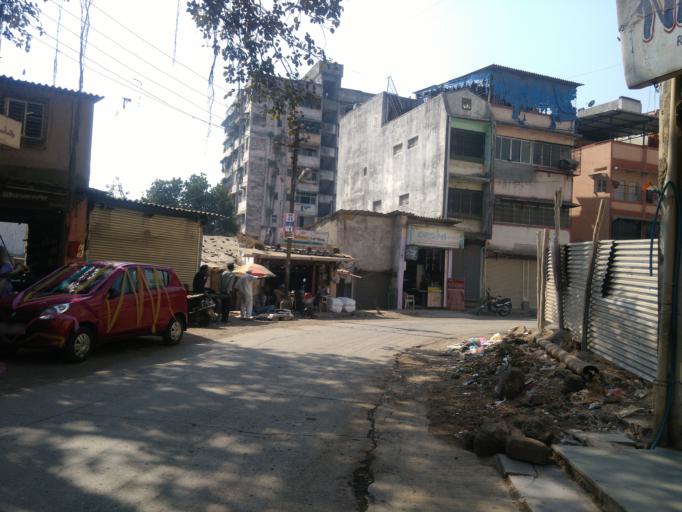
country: IN
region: Maharashtra
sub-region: Thane
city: Ulhasnagar
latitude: 19.2390
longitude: 73.1617
